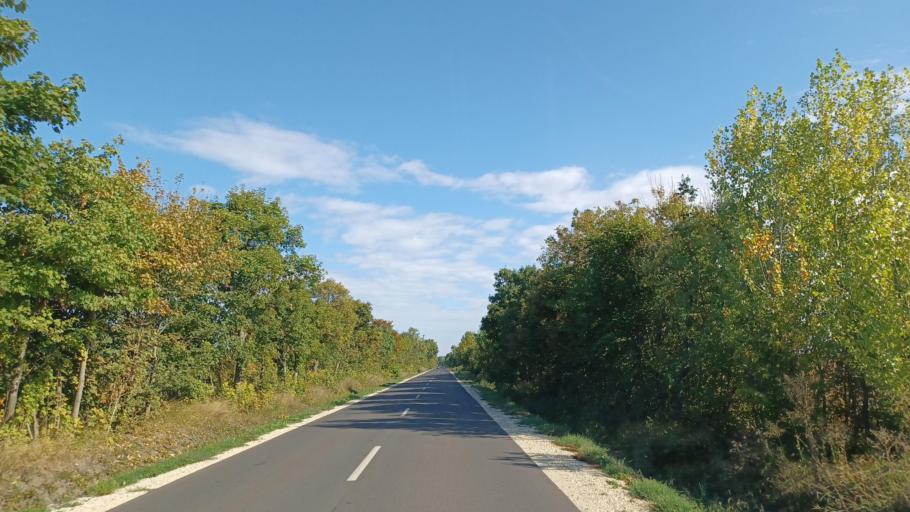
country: HU
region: Tolna
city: Dunaszentgyorgy
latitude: 46.5097
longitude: 18.8241
